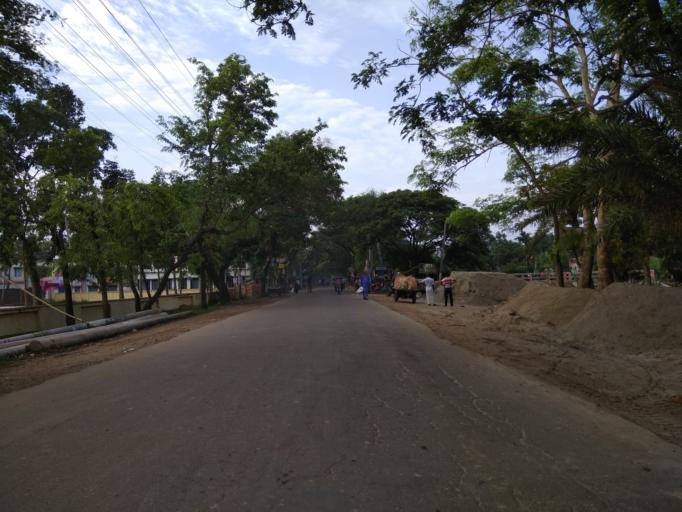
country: IN
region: West Bengal
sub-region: North 24 Parganas
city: Taki
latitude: 22.3399
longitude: 89.1058
